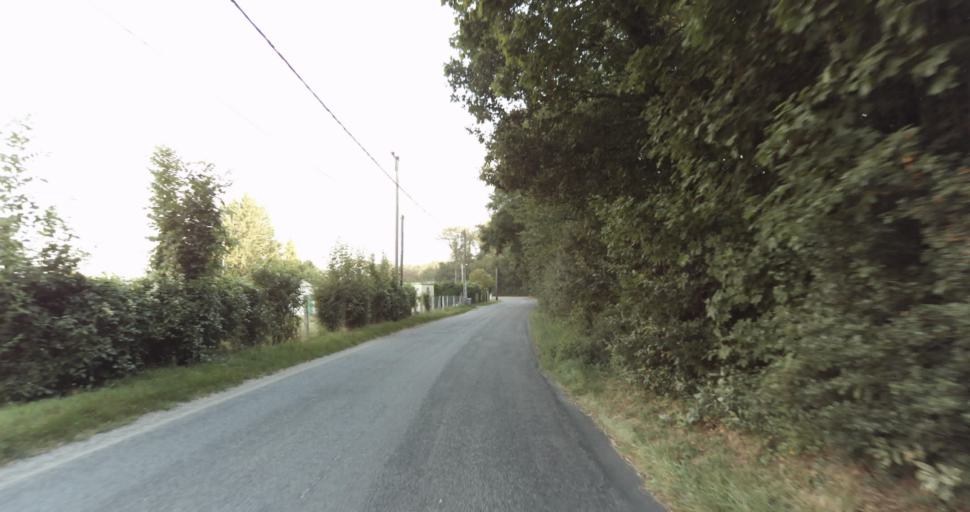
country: FR
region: Centre
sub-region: Departement d'Eure-et-Loir
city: Vert-en-Drouais
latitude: 48.7696
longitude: 1.3088
